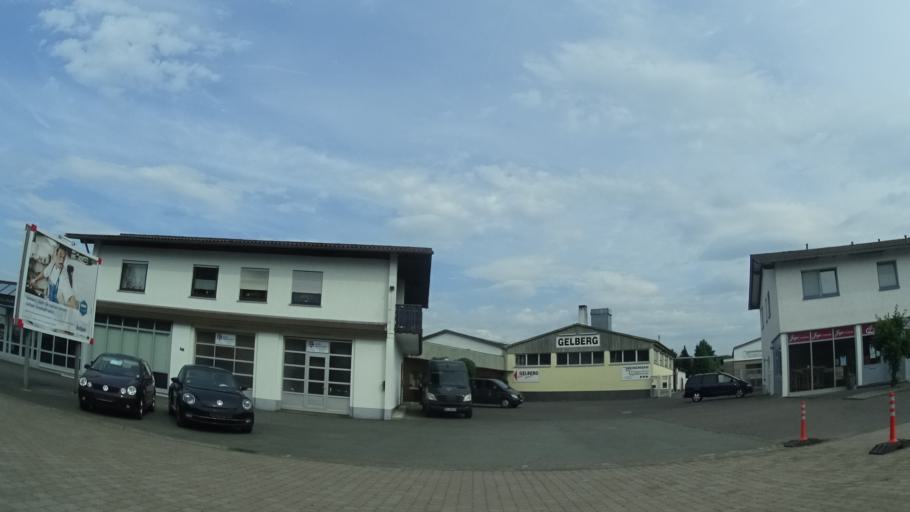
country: DE
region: Hesse
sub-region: Regierungsbezirk Kassel
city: Volkmarsen
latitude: 51.4053
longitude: 9.1128
